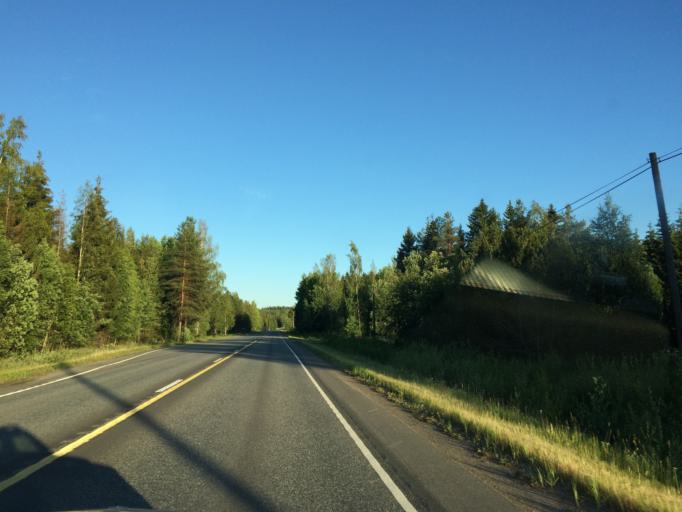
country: FI
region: Haeme
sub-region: Haemeenlinna
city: Tervakoski
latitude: 60.7755
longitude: 24.6973
